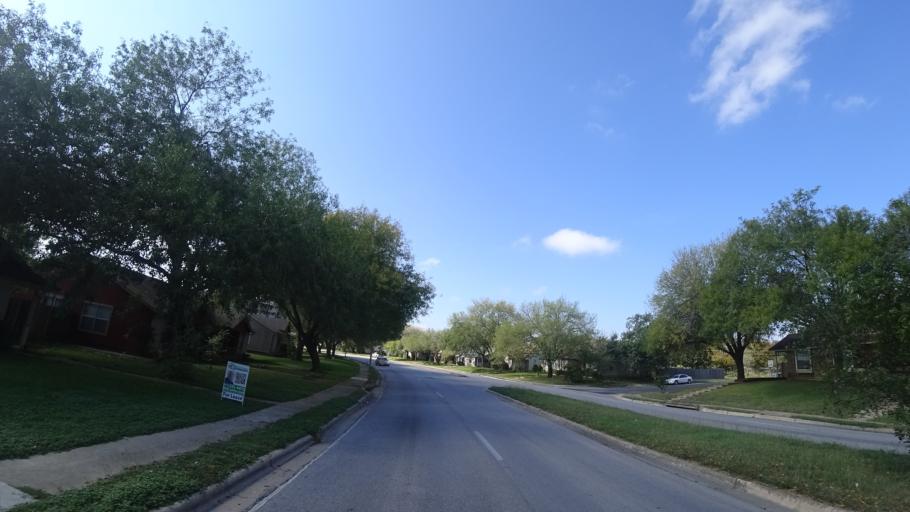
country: US
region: Texas
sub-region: Travis County
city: Shady Hollow
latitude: 30.1986
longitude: -97.8270
